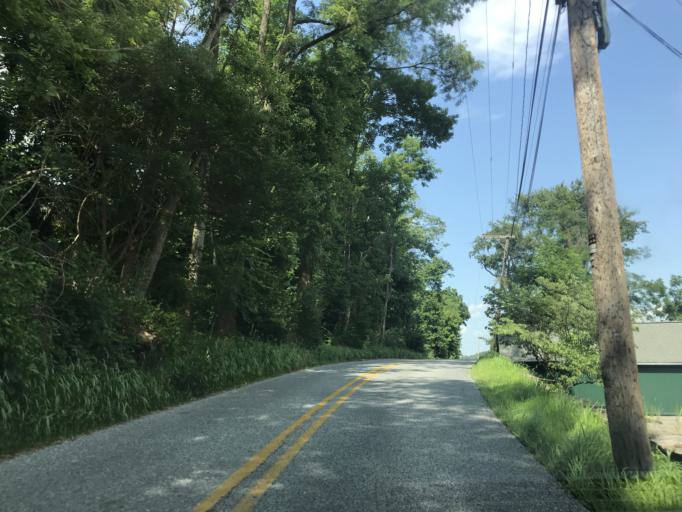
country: US
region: Delaware
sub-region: New Castle County
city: Greenville
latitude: 39.8336
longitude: -75.5842
